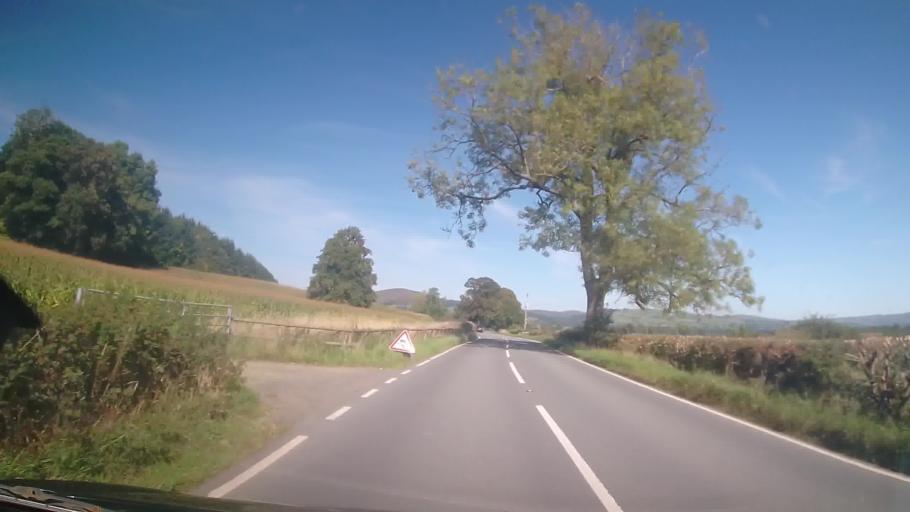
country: GB
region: England
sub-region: Shropshire
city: Lydham
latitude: 52.5018
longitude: -2.9851
